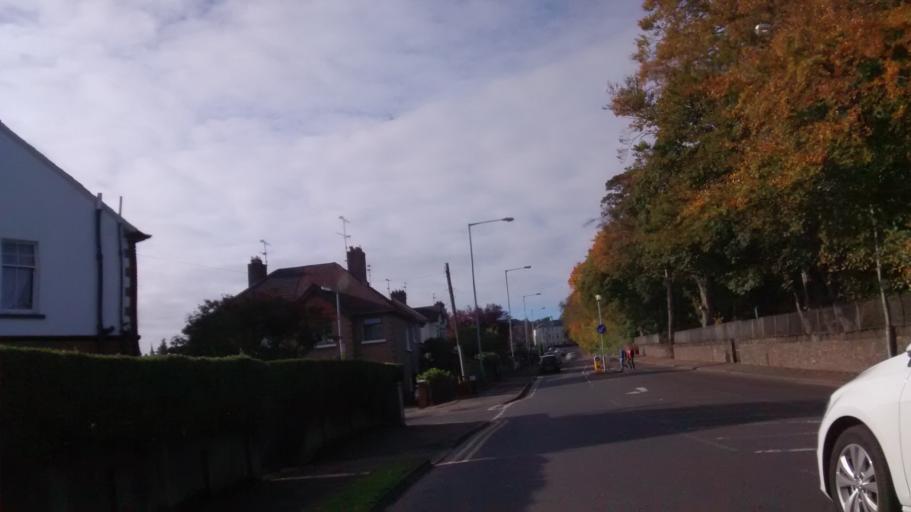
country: GB
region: Northern Ireland
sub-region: City of Derry
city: Derry
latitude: 55.0101
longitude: -7.3209
